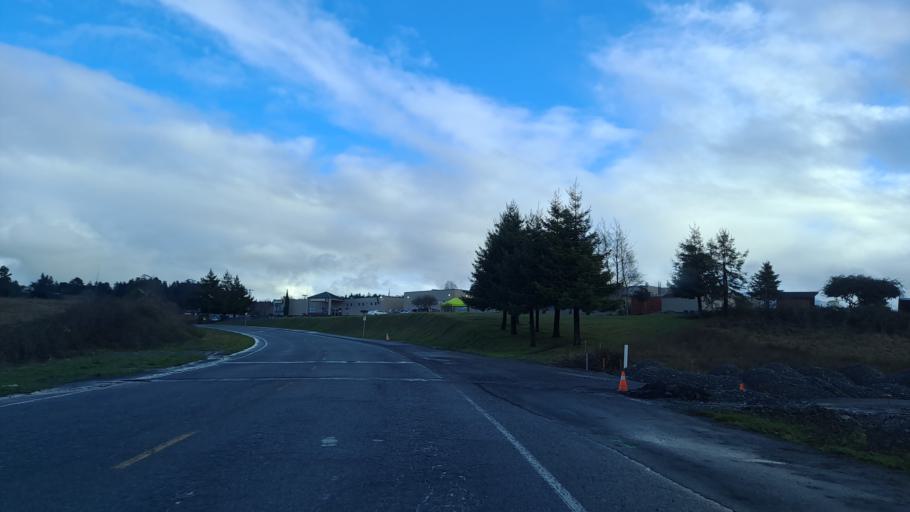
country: US
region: California
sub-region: Humboldt County
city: Fortuna
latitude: 40.5836
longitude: -124.1377
